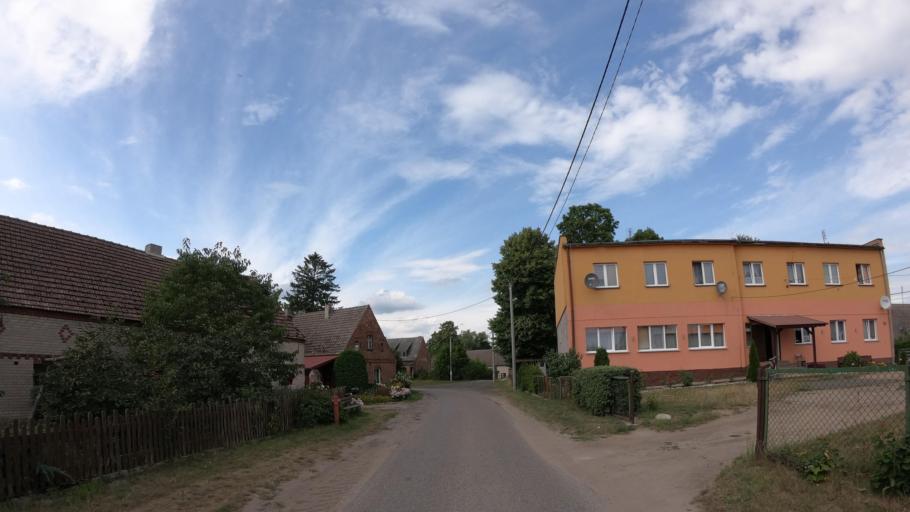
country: PL
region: West Pomeranian Voivodeship
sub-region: Powiat walecki
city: Tuczno
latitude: 53.2464
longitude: 16.1368
